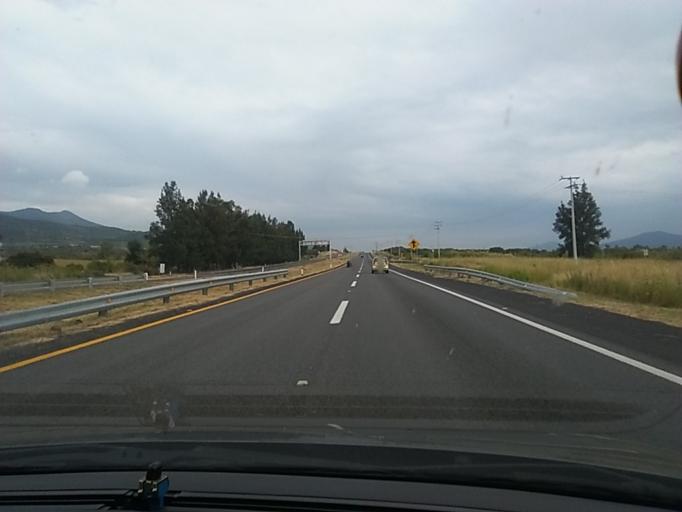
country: MX
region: Michoacan
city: Churintzio
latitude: 20.1320
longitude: -102.0692
